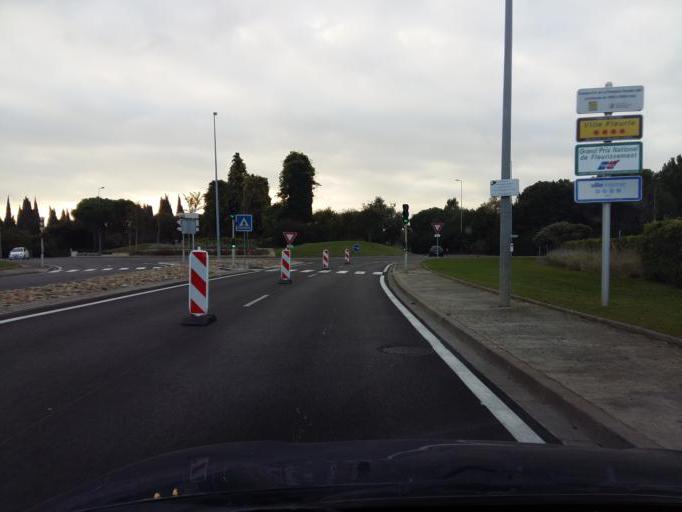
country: FR
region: Provence-Alpes-Cote d'Azur
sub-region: Departement des Bouches-du-Rhone
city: Martigues
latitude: 43.4305
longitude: 5.0468
